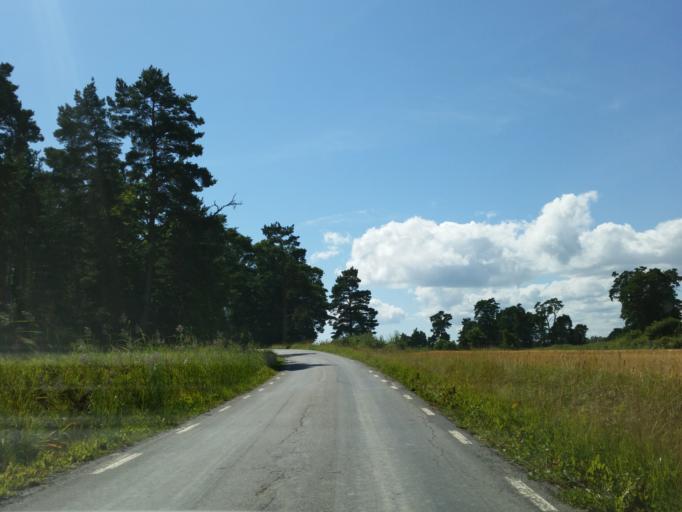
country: SE
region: Soedermanland
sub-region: Trosa Kommun
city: Trosa
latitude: 58.9730
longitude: 17.6510
